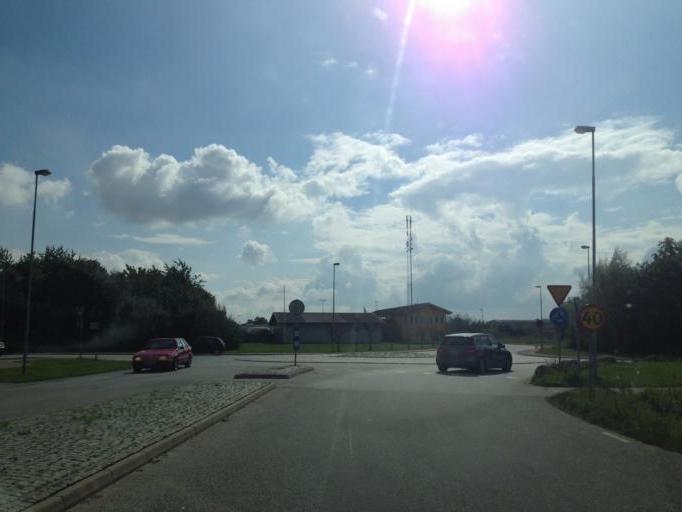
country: SE
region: Skane
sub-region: Lomma Kommun
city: Lomma
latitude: 55.6827
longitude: 13.0847
